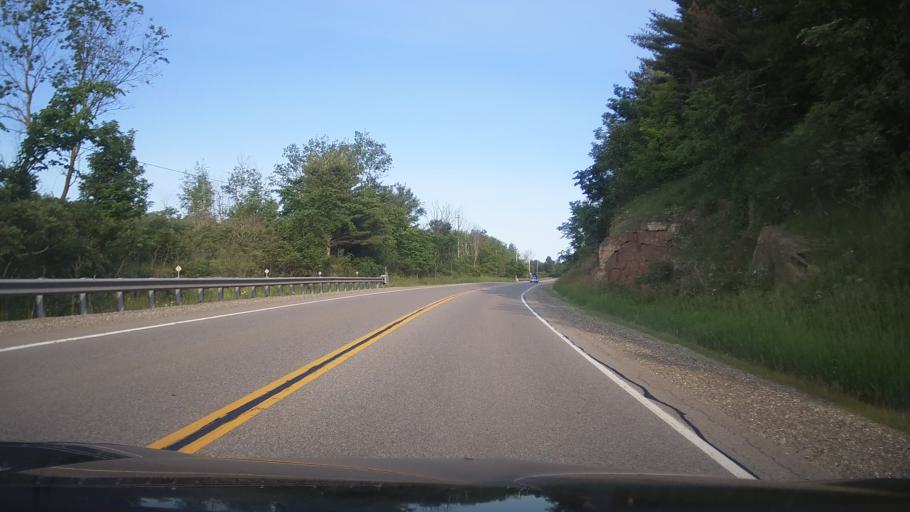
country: CA
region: Ontario
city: Perth
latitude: 44.8200
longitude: -76.6077
